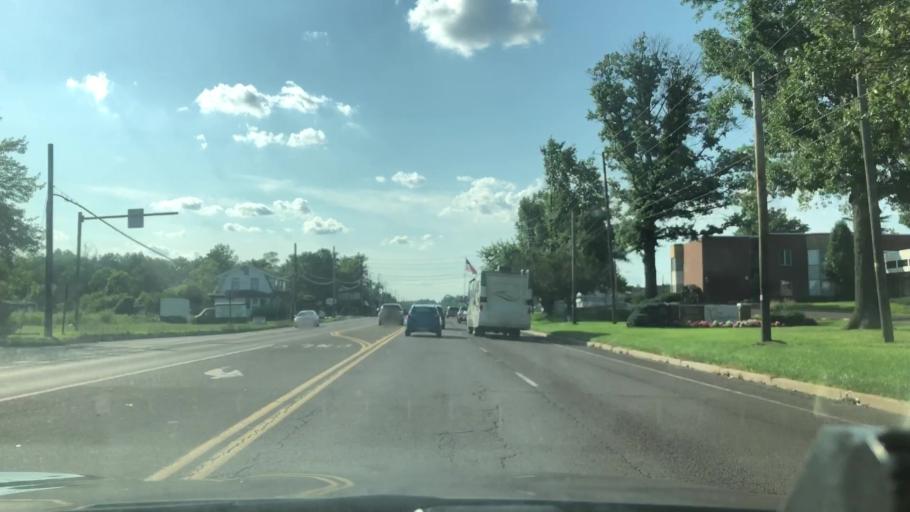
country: US
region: Pennsylvania
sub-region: Montgomery County
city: Hatfield
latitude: 40.2987
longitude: -75.2845
